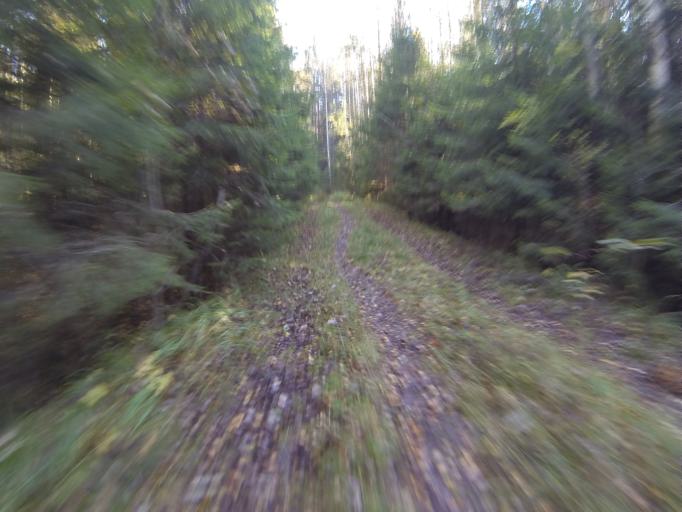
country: FI
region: Varsinais-Suomi
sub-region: Salo
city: Saerkisalo
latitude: 60.2145
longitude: 22.9704
